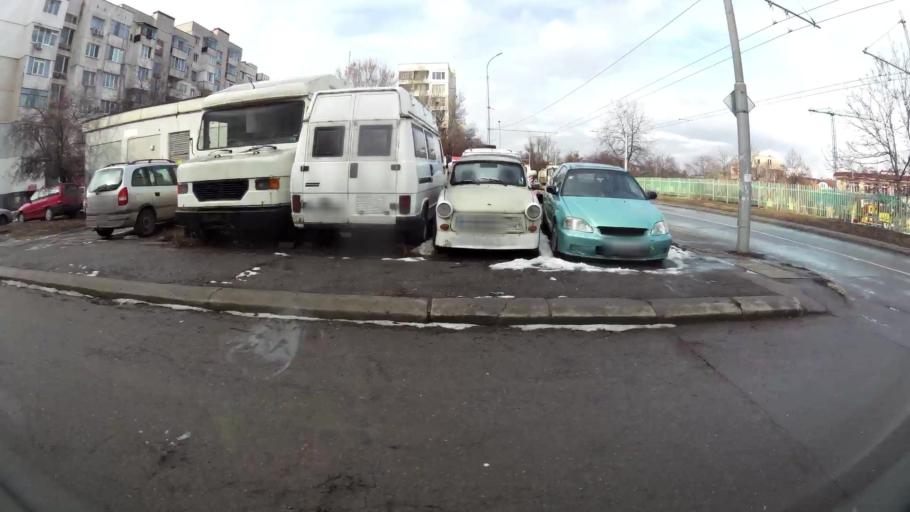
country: BG
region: Sofia-Capital
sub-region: Stolichna Obshtina
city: Sofia
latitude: 42.7171
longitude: 23.2746
